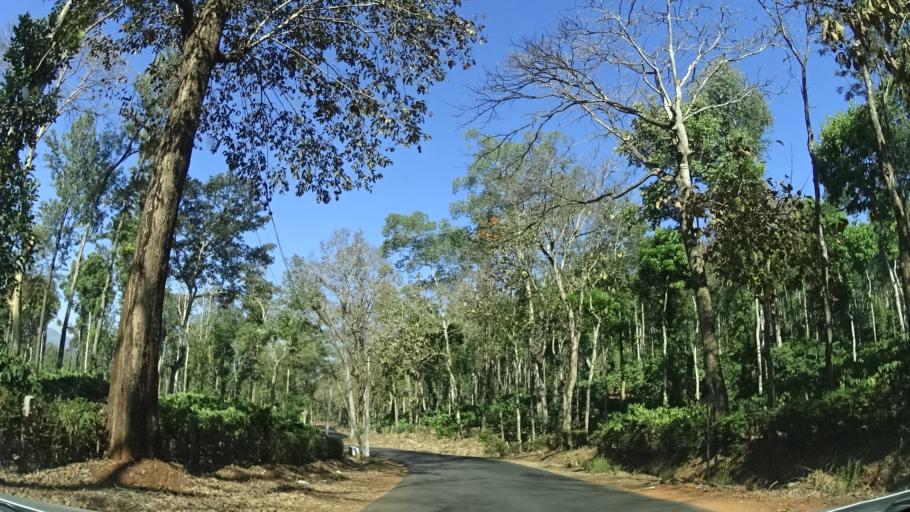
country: IN
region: Karnataka
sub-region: Chikmagalur
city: Koppa
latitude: 13.3485
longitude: 75.4824
